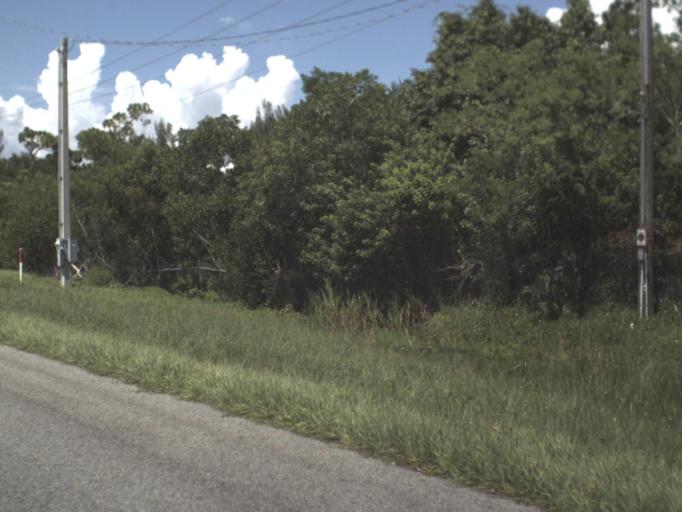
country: US
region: Florida
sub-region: Charlotte County
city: Punta Gorda
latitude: 26.9416
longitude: -82.0162
